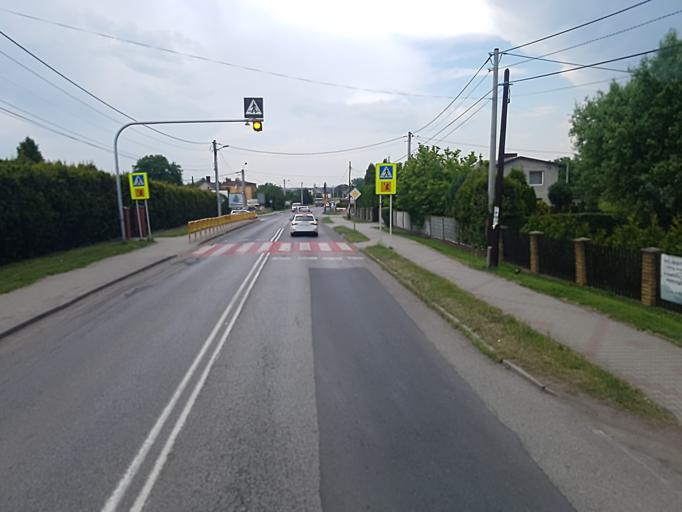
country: PL
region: Silesian Voivodeship
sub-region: Powiat wodzislawski
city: Wodzislaw Slaski
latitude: 49.9907
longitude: 18.4940
